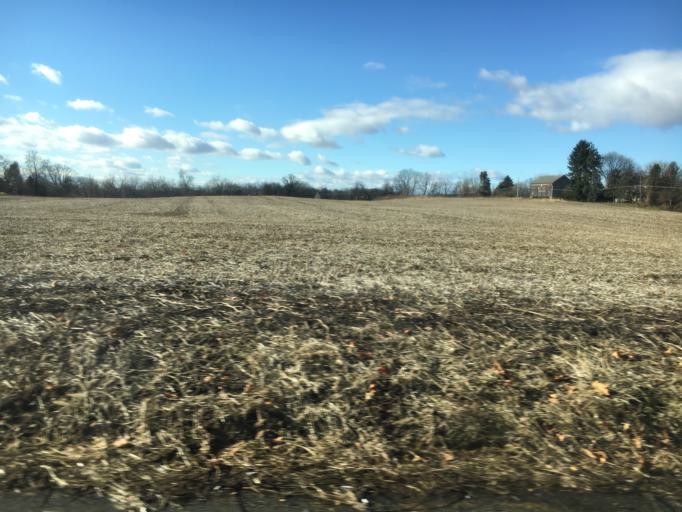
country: US
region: Pennsylvania
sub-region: Lehigh County
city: Egypt
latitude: 40.6453
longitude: -75.5478
